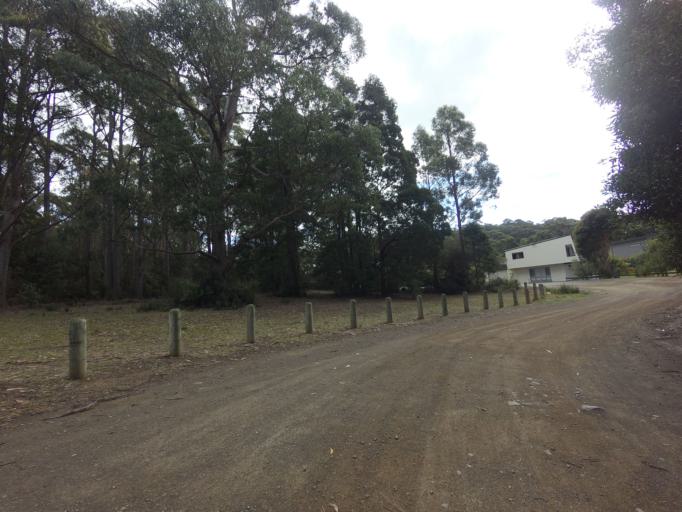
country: AU
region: Tasmania
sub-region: Clarence
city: Sandford
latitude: -43.1373
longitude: 147.8536
